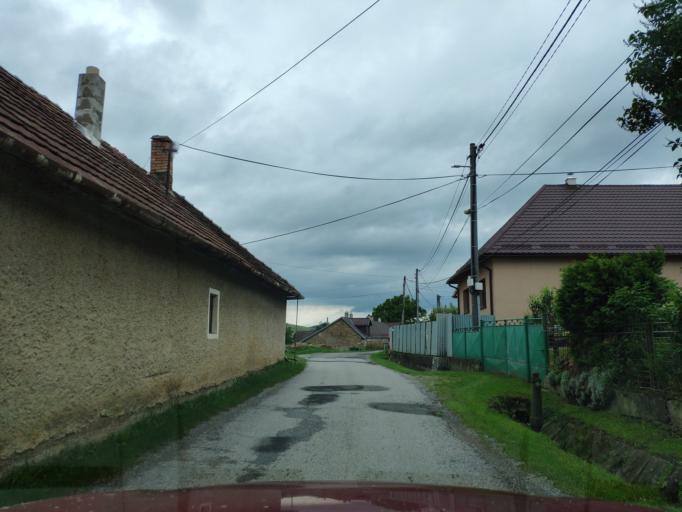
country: SK
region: Presovsky
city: Sabinov
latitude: 49.0473
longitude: 21.0148
